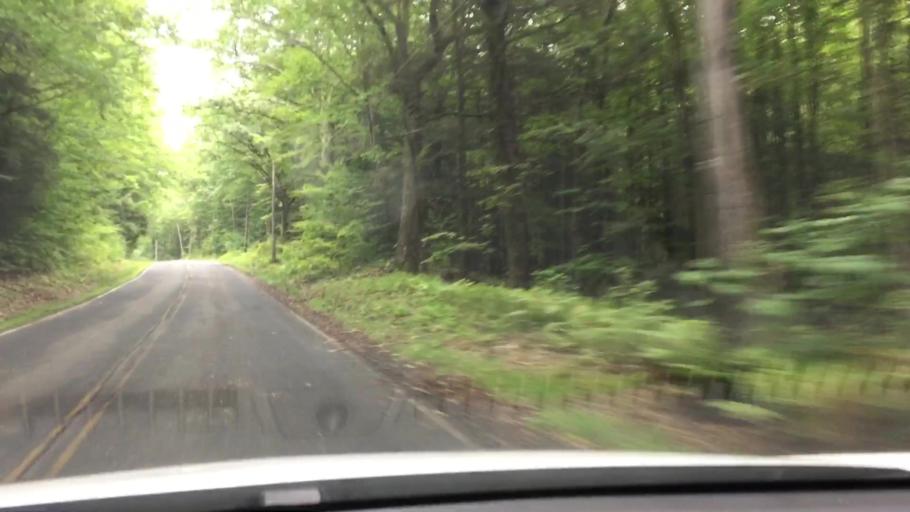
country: US
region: Massachusetts
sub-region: Berkshire County
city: Otis
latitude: 42.2479
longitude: -72.9898
